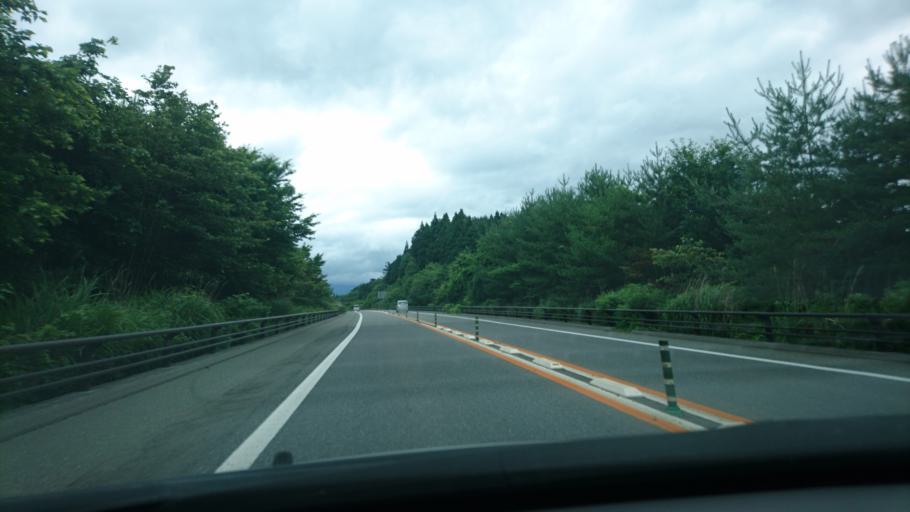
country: JP
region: Iwate
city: Ofunato
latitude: 39.0434
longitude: 141.7155
